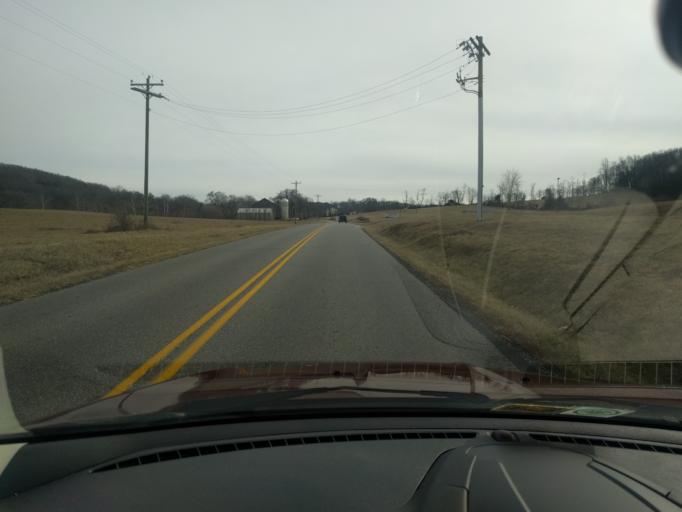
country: US
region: Virginia
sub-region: Augusta County
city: Fishersville
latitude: 38.0834
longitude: -78.9741
